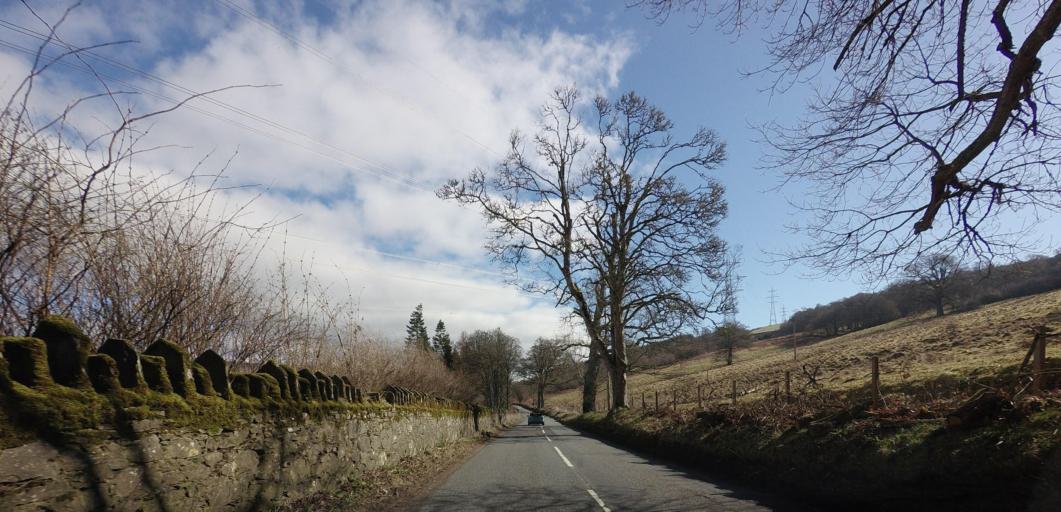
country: GB
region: Scotland
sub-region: Perth and Kinross
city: Aberfeldy
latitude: 56.6049
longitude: -3.9537
